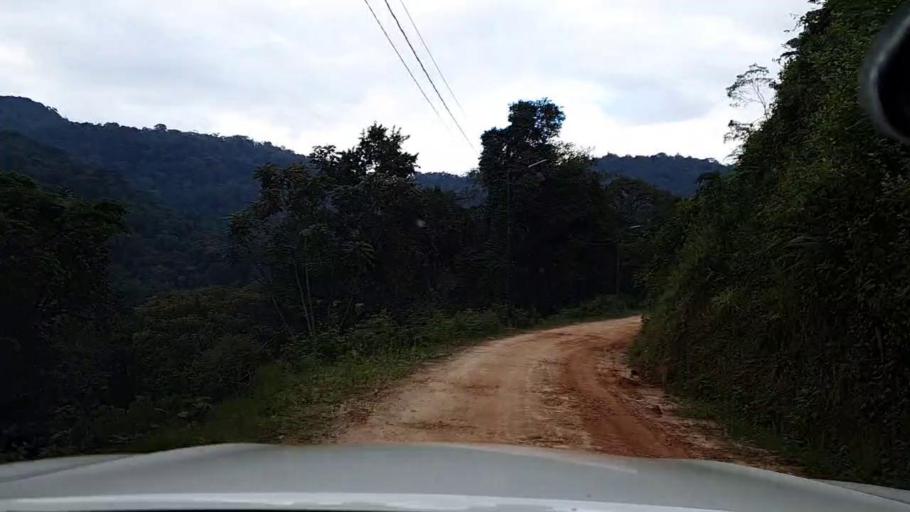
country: RW
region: Western Province
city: Cyangugu
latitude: -2.5604
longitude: 29.2285
